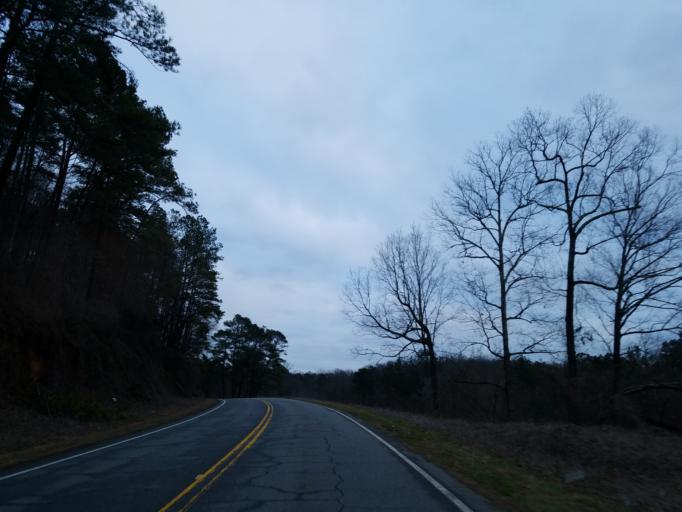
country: US
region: Georgia
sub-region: Bartow County
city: Emerson
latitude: 34.1034
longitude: -84.7414
